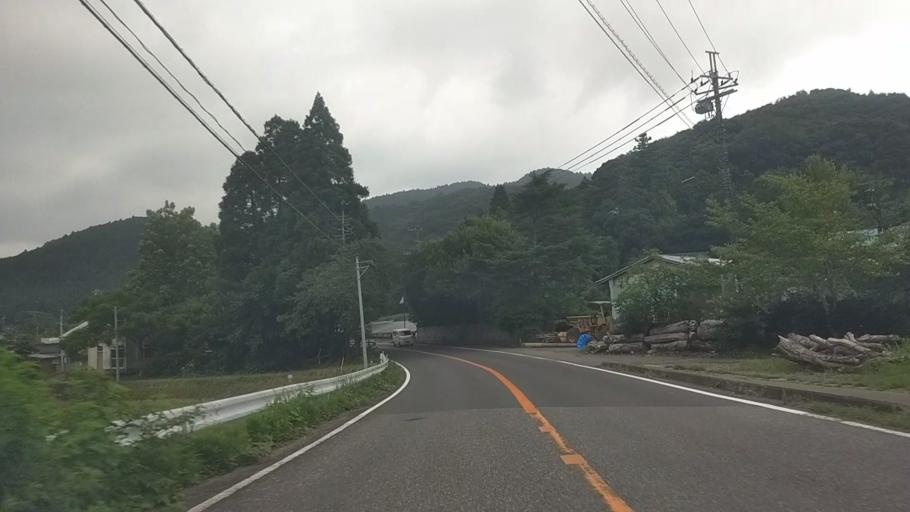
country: JP
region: Chiba
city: Kawaguchi
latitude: 35.1415
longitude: 139.9729
